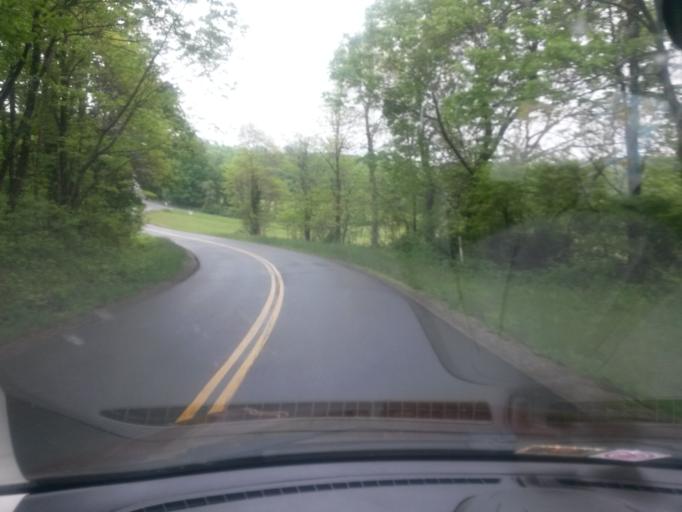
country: US
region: Virginia
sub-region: Floyd County
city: Floyd
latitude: 36.7763
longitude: -80.3918
